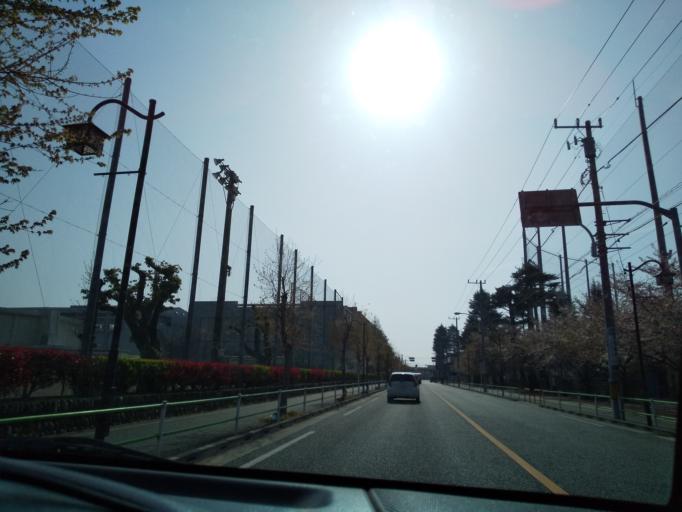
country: JP
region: Tokyo
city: Hino
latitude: 35.7040
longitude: 139.3856
